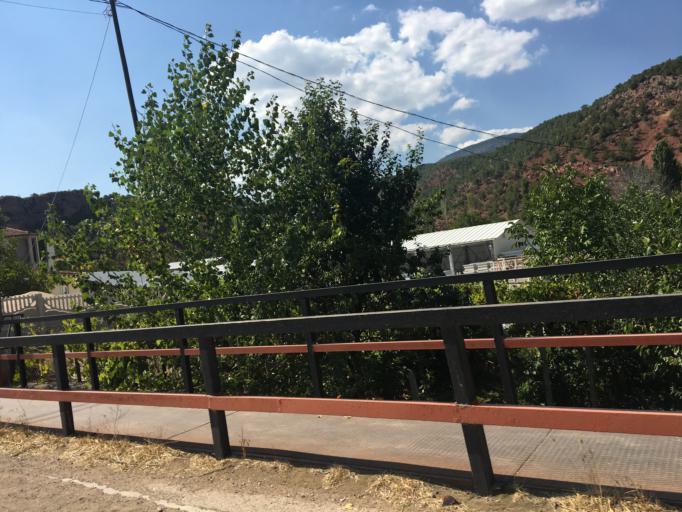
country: TR
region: Ankara
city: Nallihan
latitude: 40.1774
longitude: 31.3417
